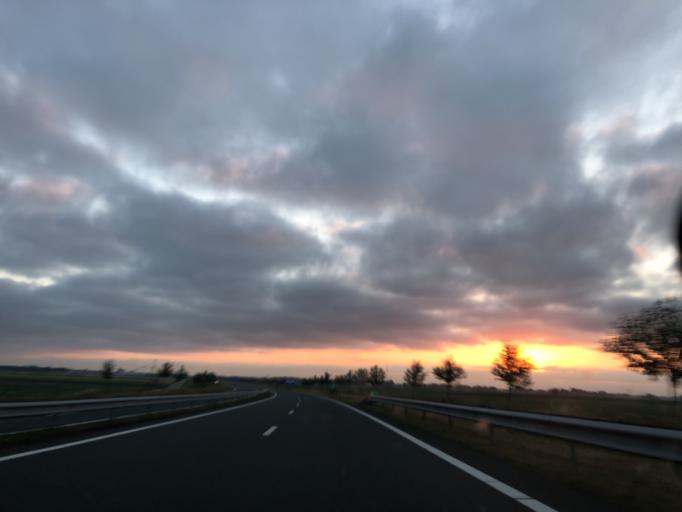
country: NL
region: Groningen
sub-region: Gemeente Veendam
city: Veendam
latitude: 53.0632
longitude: 6.8727
